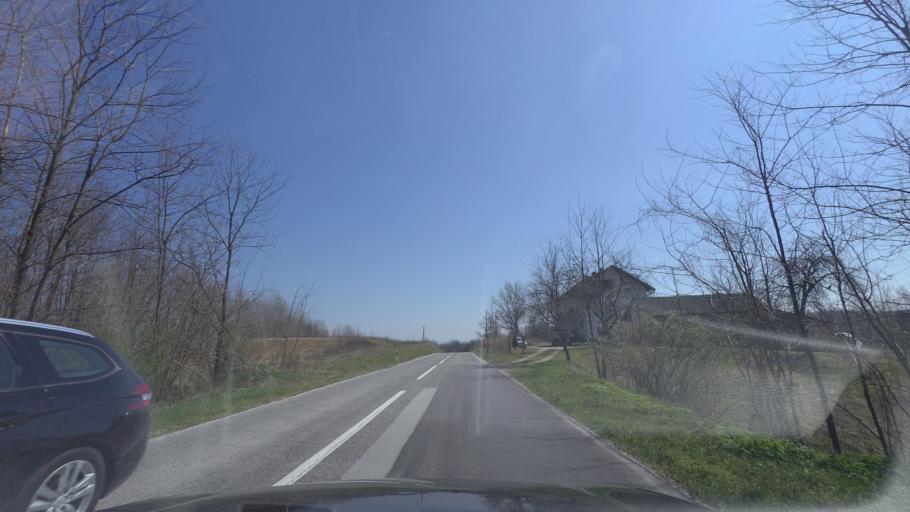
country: HR
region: Sisacko-Moslavacka
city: Gvozd
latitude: 45.3439
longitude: 15.8913
